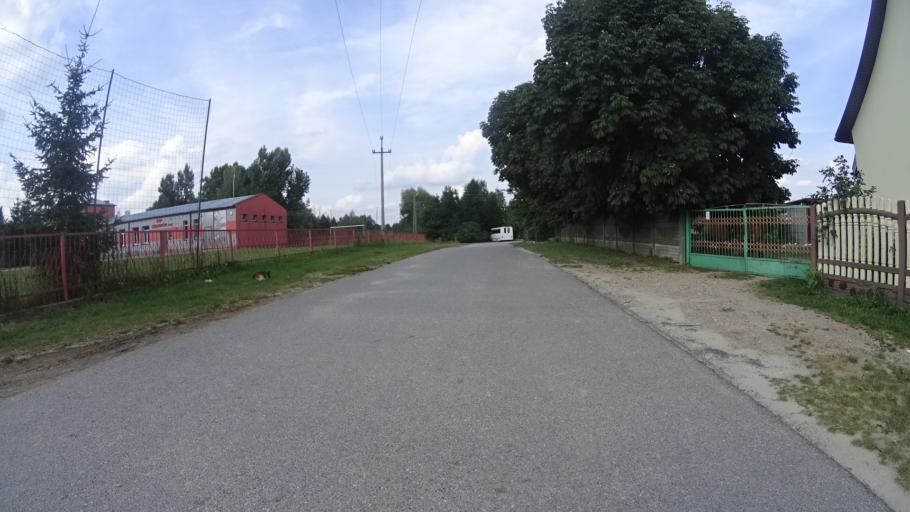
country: PL
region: Masovian Voivodeship
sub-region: Powiat grojecki
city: Mogielnica
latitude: 51.6572
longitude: 20.7571
